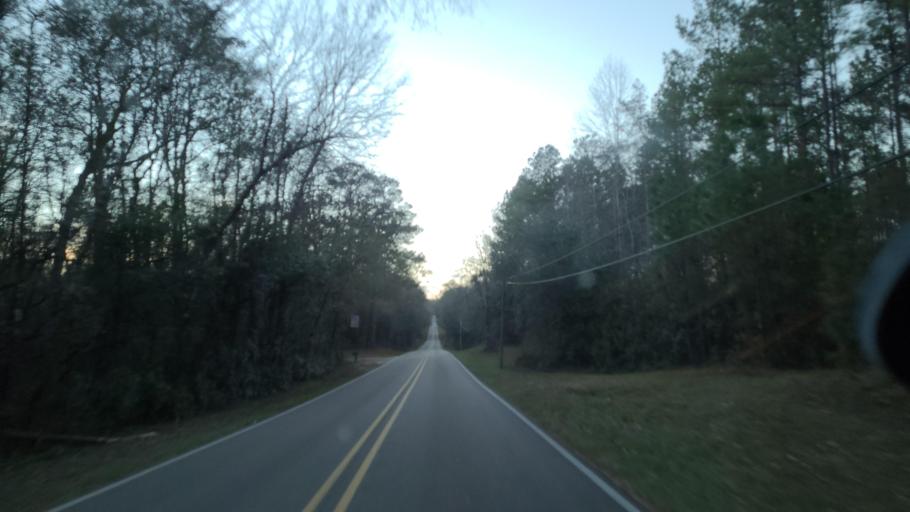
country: US
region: Mississippi
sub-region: Forrest County
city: Hattiesburg
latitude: 31.1676
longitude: -89.2353
